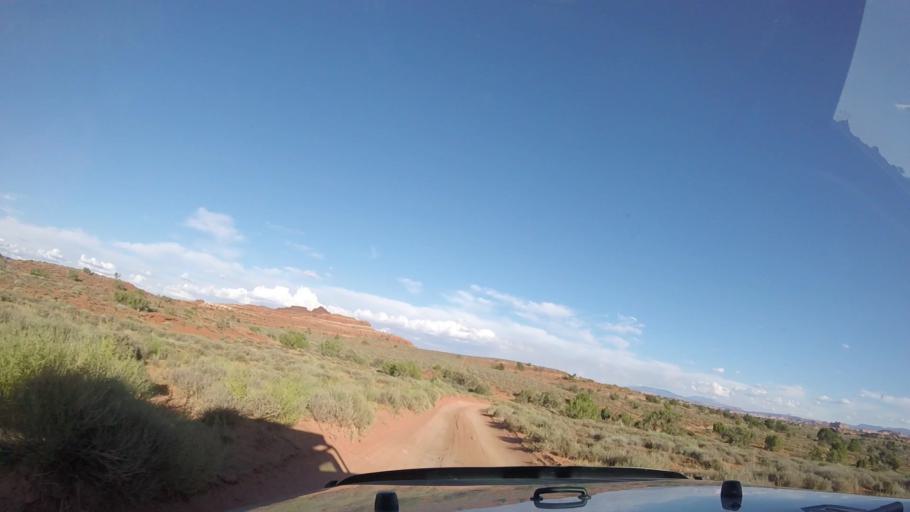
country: US
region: Utah
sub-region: Grand County
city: Moab
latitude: 38.2120
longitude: -109.7884
